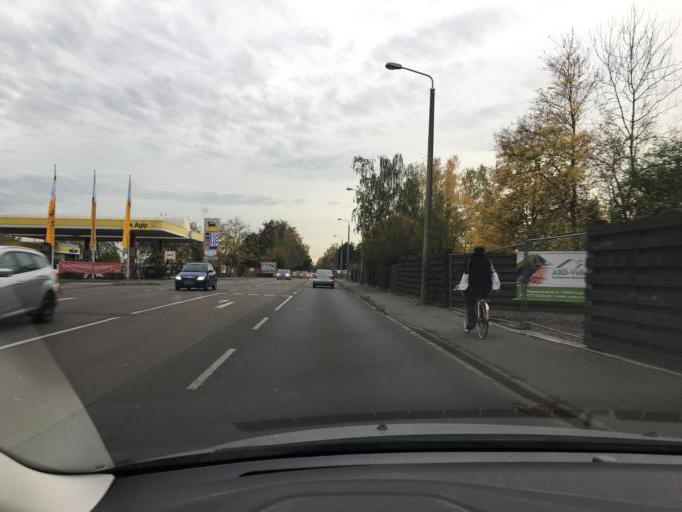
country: DE
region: Saxony
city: Taucha
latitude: 51.3396
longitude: 12.4450
